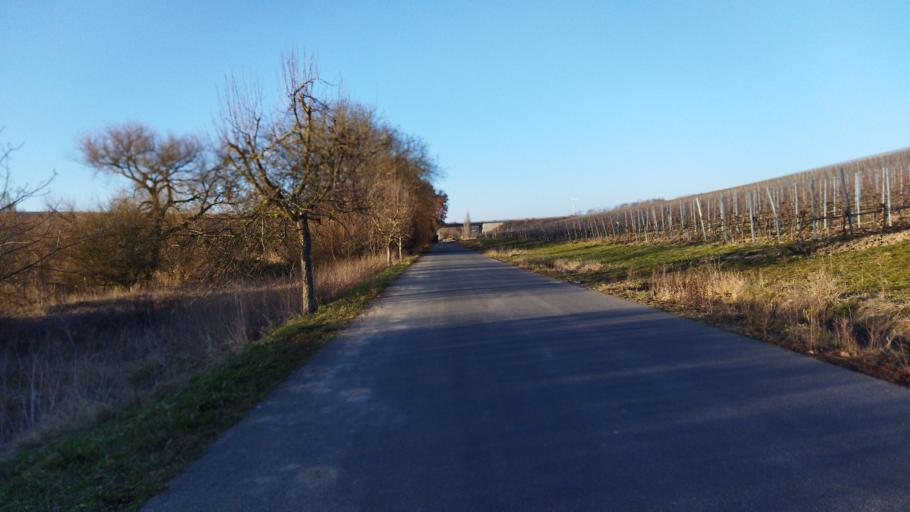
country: DE
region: Bavaria
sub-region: Regierungsbezirk Unterfranken
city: Mainstockheim
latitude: 49.7799
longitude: 10.1566
